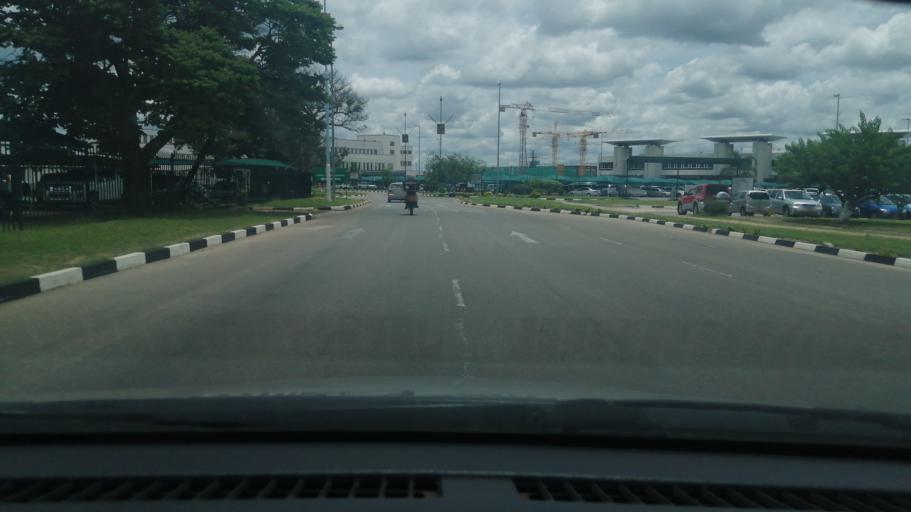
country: ZW
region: Harare
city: Epworth
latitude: -17.9169
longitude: 31.0998
